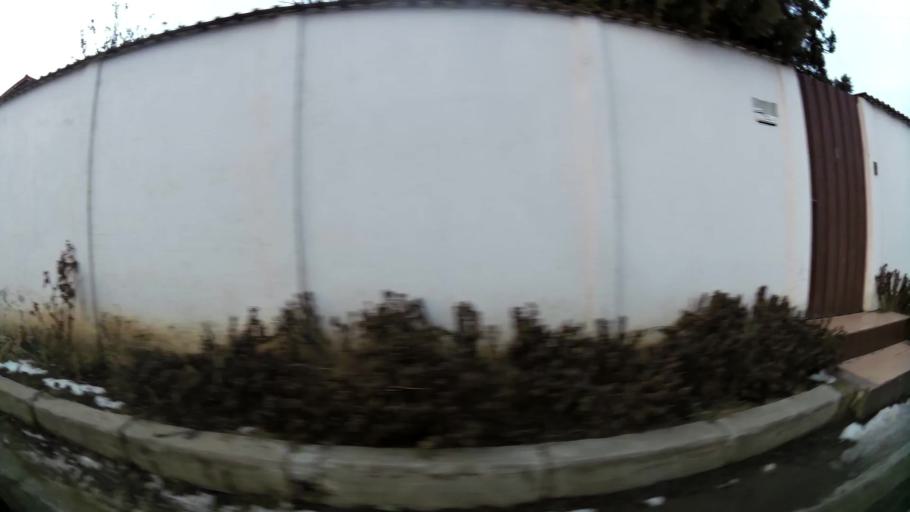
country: RO
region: Ilfov
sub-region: Comuna Magurele
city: Magurele
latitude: 44.3906
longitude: 26.0241
